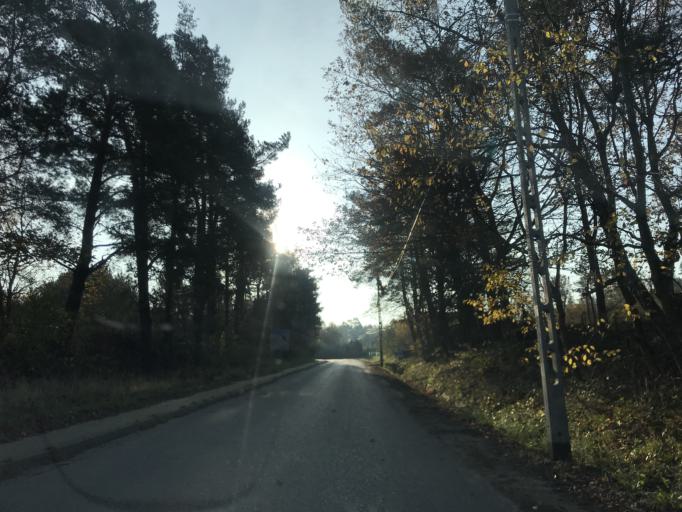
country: PL
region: Pomeranian Voivodeship
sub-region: Powiat pucki
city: Krokowa
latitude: 54.7998
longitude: 18.1102
